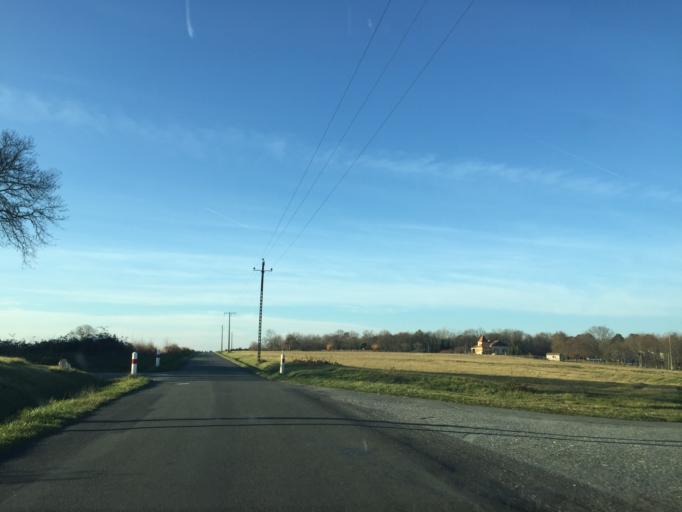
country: FR
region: Aquitaine
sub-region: Departement de la Dordogne
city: Riberac
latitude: 45.2117
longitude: 0.2995
